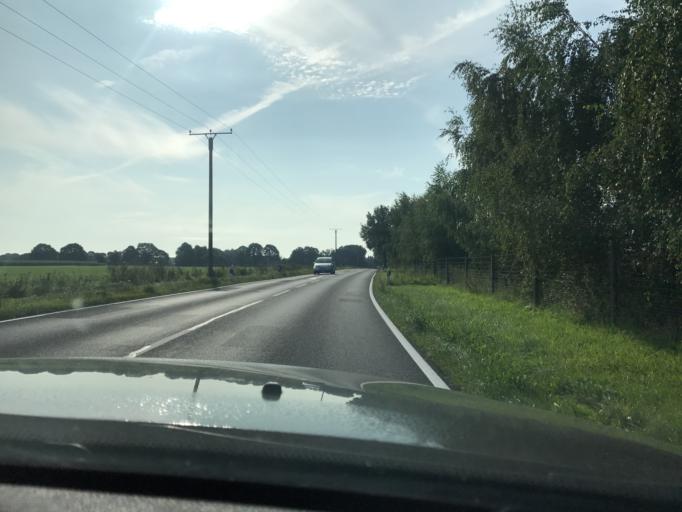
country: DE
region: Lower Saxony
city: Bawinkel
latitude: 52.6661
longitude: 7.4082
